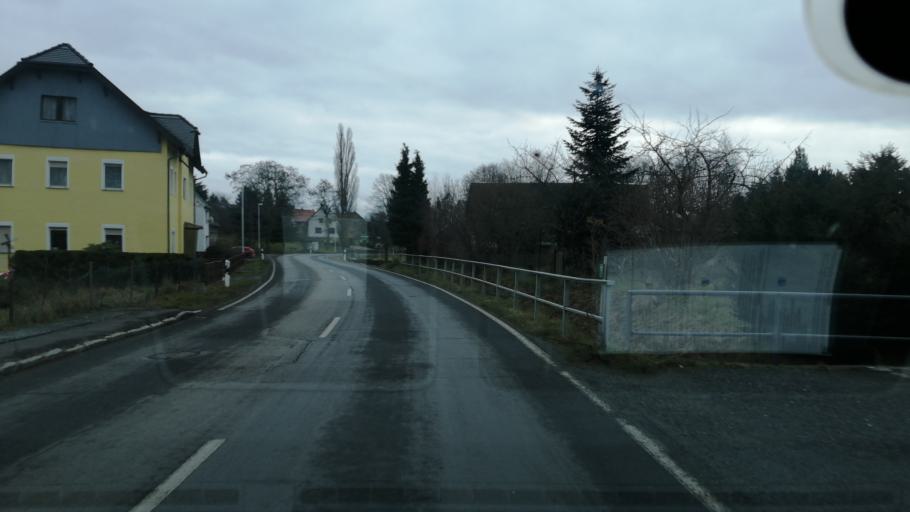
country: DE
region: Saxony
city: Sohland am Rotstein
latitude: 51.0694
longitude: 14.7799
